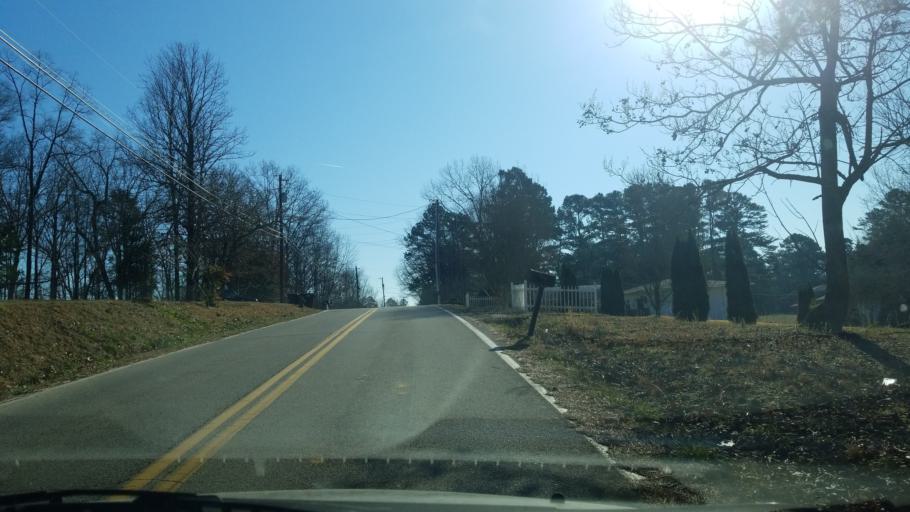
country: US
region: Tennessee
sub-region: Hamilton County
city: Harrison
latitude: 35.0648
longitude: -85.1081
